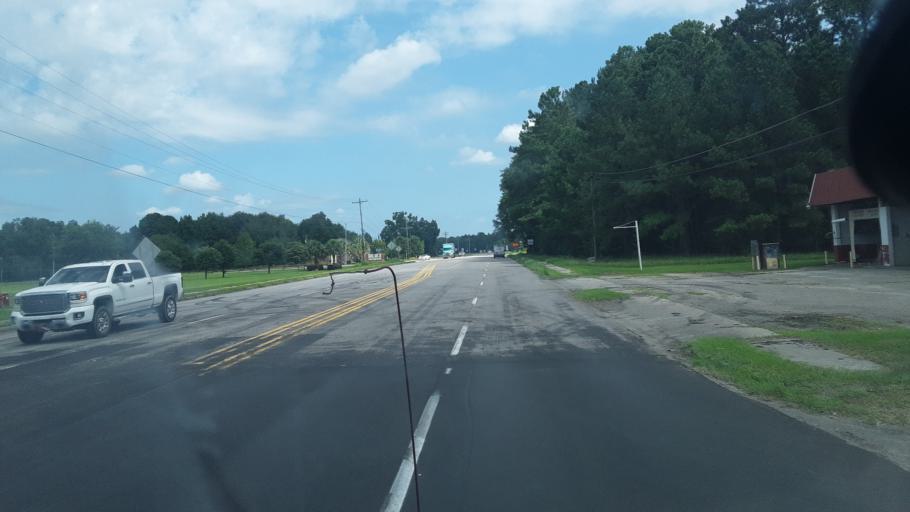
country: US
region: South Carolina
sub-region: Bamberg County
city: Bamberg
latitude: 33.3111
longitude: -81.0343
